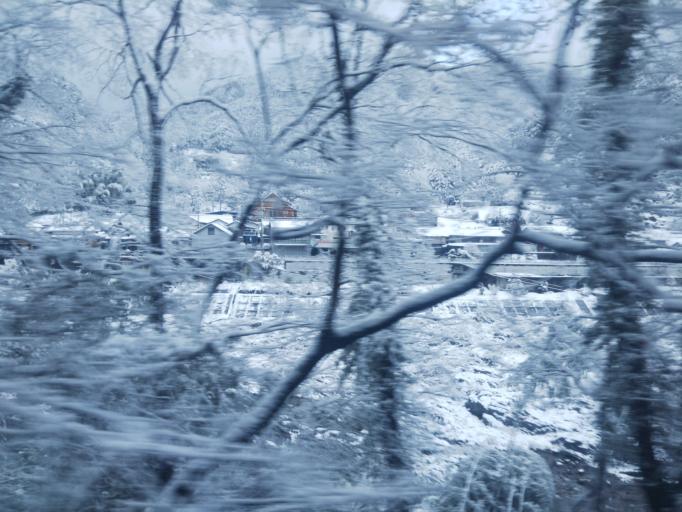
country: JP
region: Tokushima
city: Ikedacho
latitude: 33.7846
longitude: 133.7193
